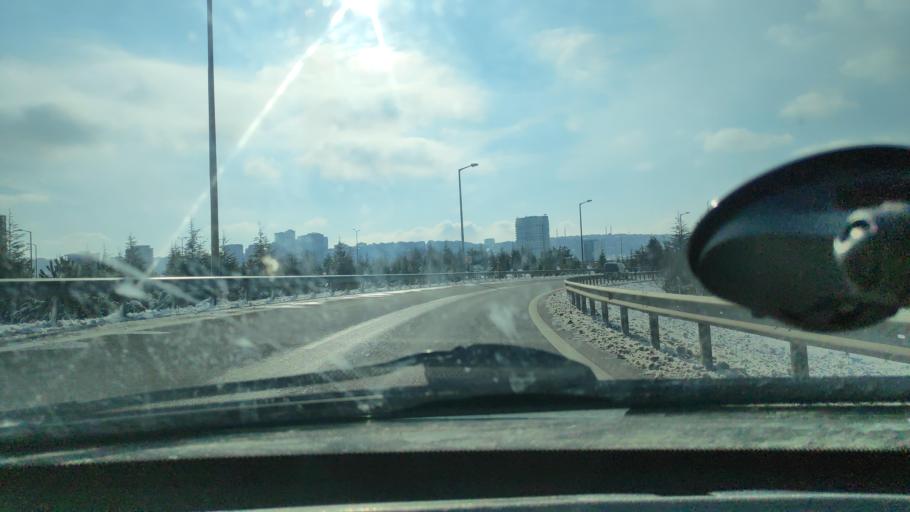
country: TR
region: Ankara
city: Ankara
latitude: 40.0244
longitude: 32.8279
